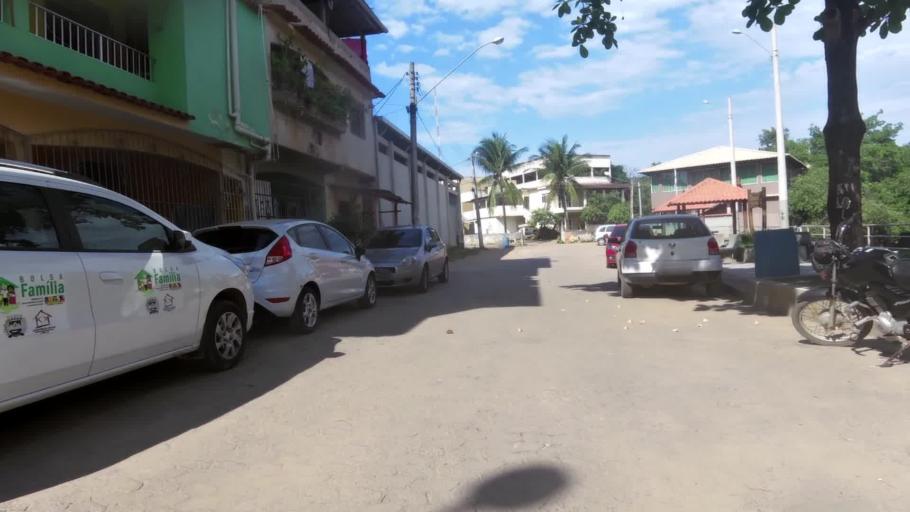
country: BR
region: Espirito Santo
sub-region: Piuma
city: Piuma
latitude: -20.8376
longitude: -40.7292
